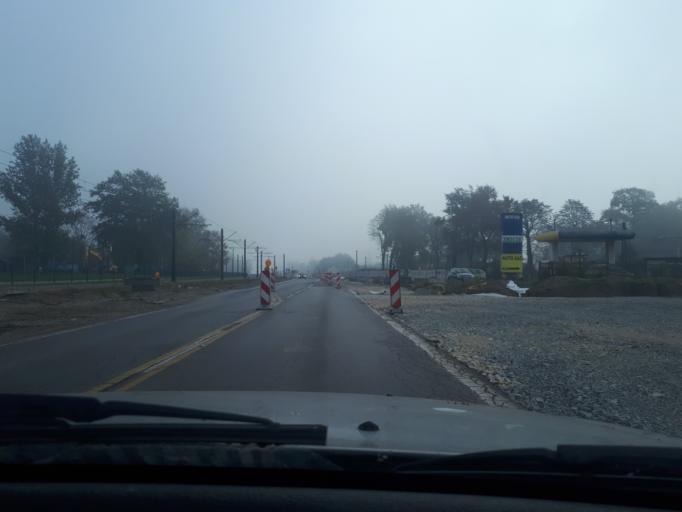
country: PL
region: Lesser Poland Voivodeship
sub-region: Powiat wielicki
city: Wegrzce Wielkie
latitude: 50.0723
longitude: 20.1140
